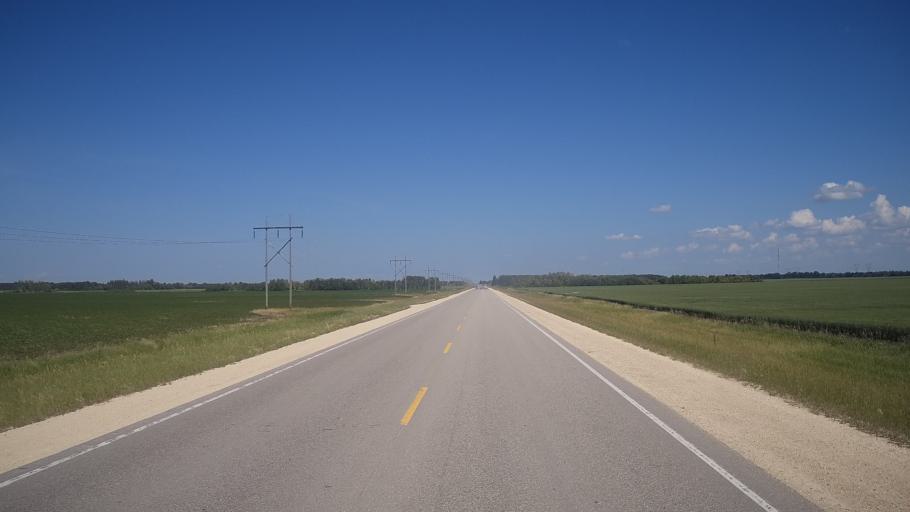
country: CA
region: Manitoba
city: Stonewall
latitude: 50.1227
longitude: -97.3778
